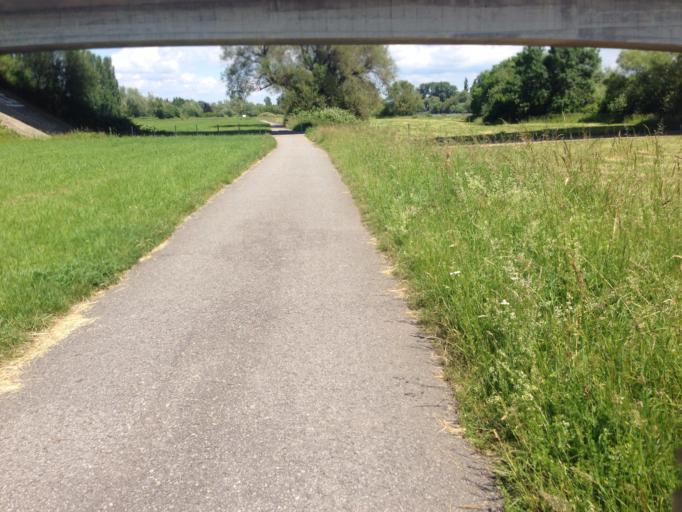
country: DE
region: Hesse
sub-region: Regierungsbezirk Darmstadt
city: Grosskrotzenburg
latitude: 50.0934
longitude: 8.9415
